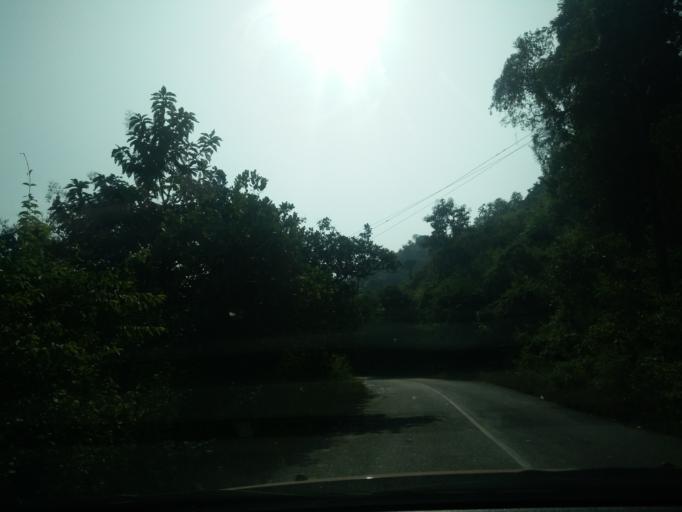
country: IN
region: Goa
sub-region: North Goa
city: Palle
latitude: 15.4621
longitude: 74.0756
